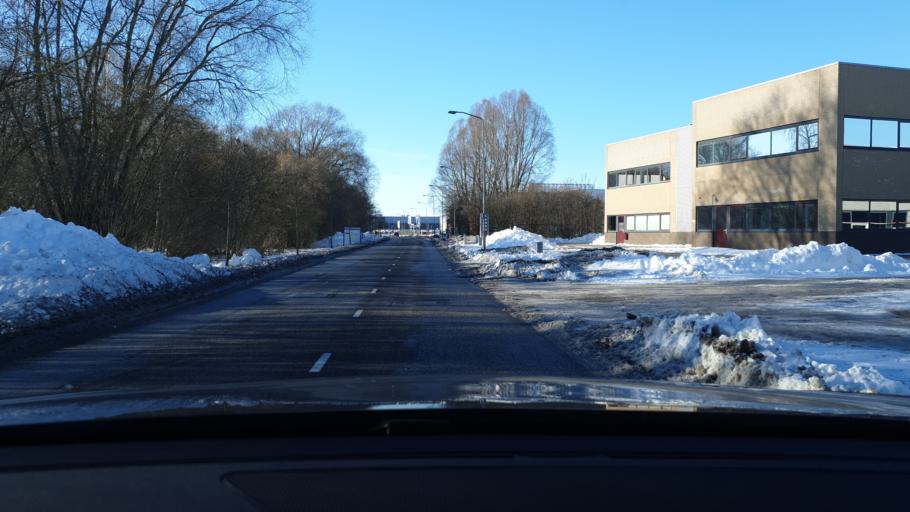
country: NL
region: Gelderland
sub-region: Gemeente Nijmegen
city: Lindenholt
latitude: 51.8219
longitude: 5.7620
